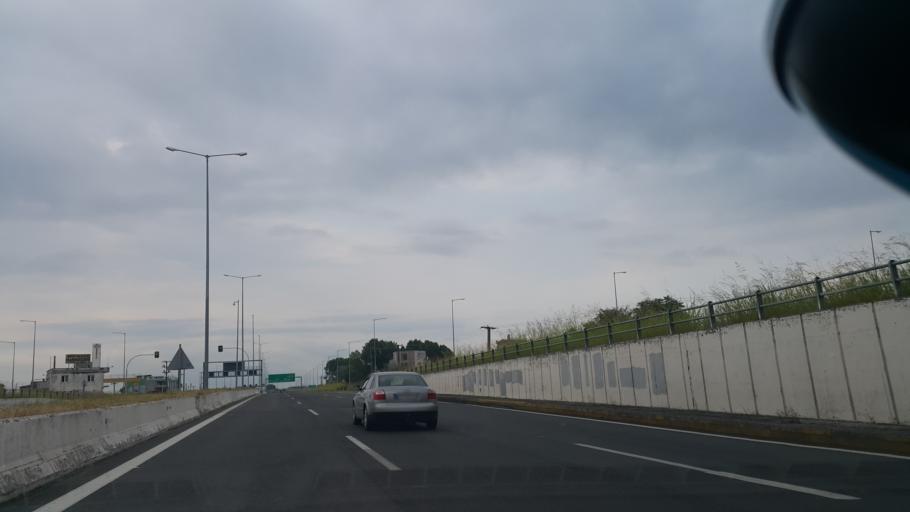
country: GR
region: Central Macedonia
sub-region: Nomos Pierias
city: Peristasi
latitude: 40.2644
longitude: 22.5271
